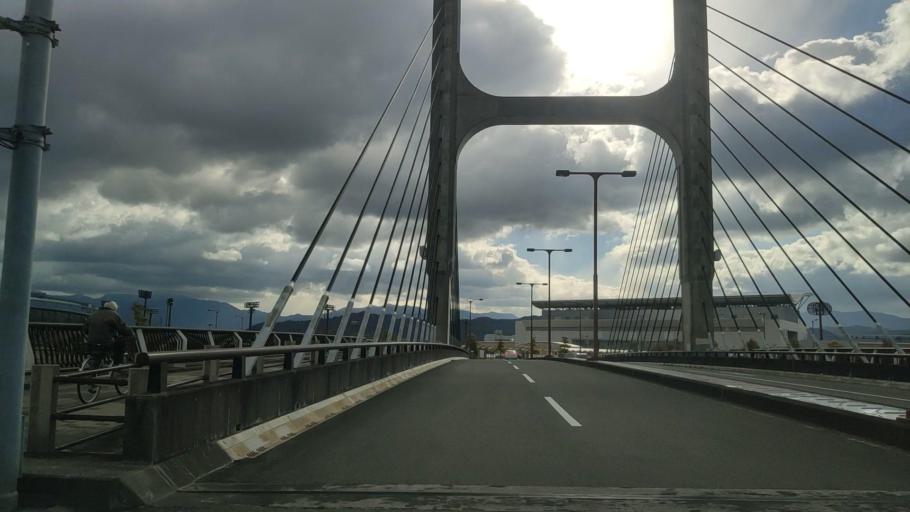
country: JP
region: Ehime
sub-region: Shikoku-chuo Shi
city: Matsuyama
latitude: 33.8110
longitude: 132.7417
